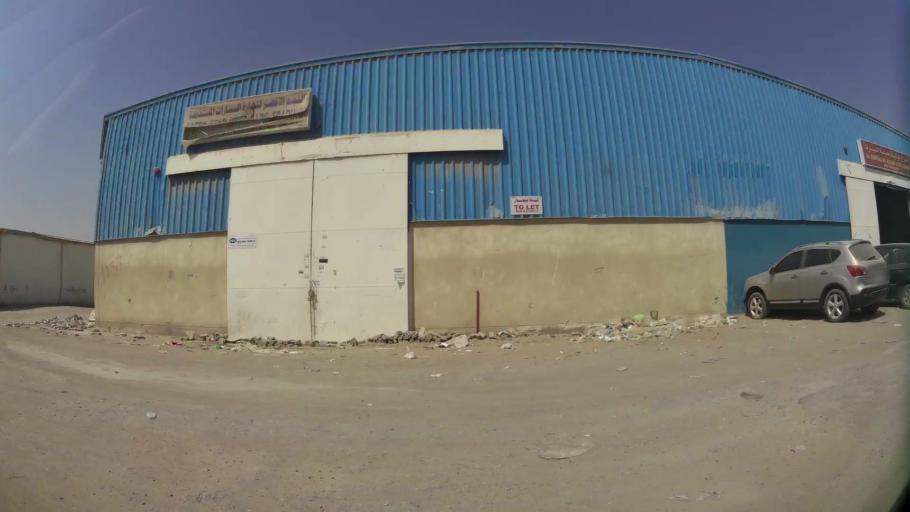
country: AE
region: Ash Shariqah
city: Sharjah
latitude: 25.3089
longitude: 55.3872
